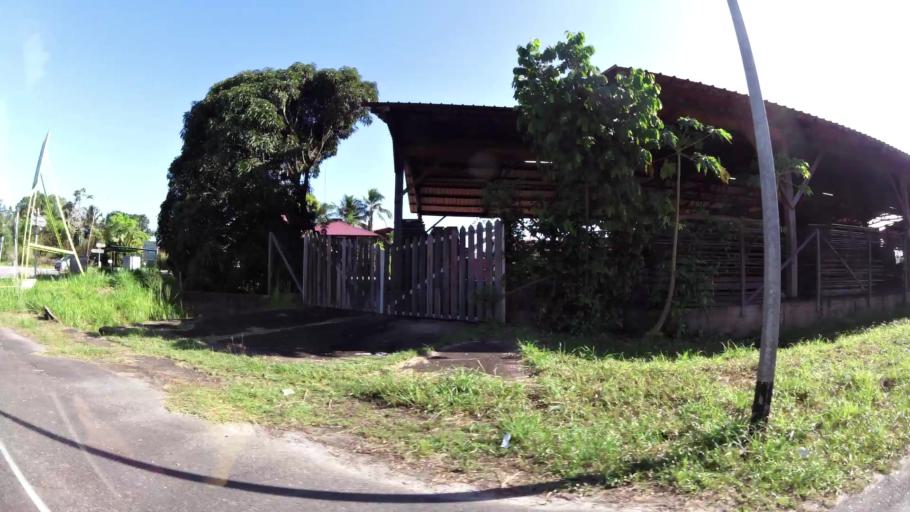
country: GF
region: Guyane
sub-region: Guyane
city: Matoury
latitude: 4.8592
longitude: -52.2715
